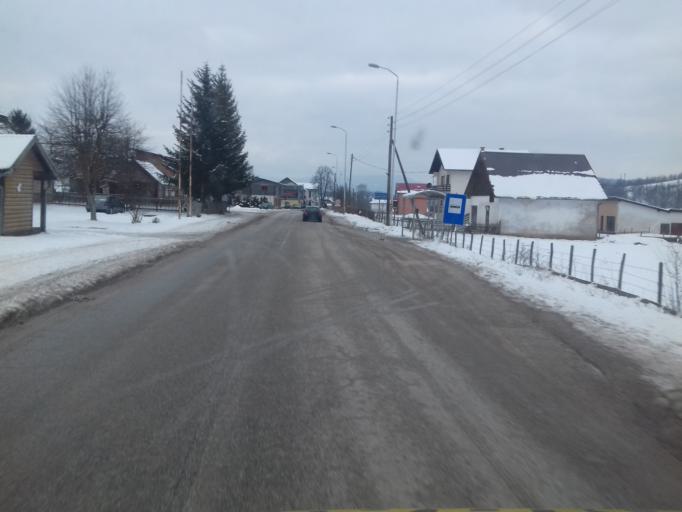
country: BA
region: Republika Srpska
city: Pale
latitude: 43.8828
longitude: 18.6087
